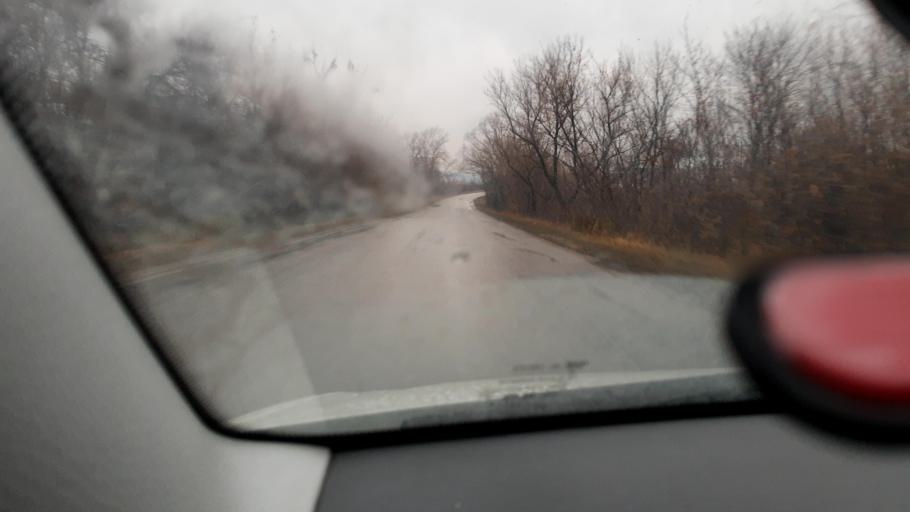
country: RU
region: Bashkortostan
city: Ufa
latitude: 54.8733
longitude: 56.1310
